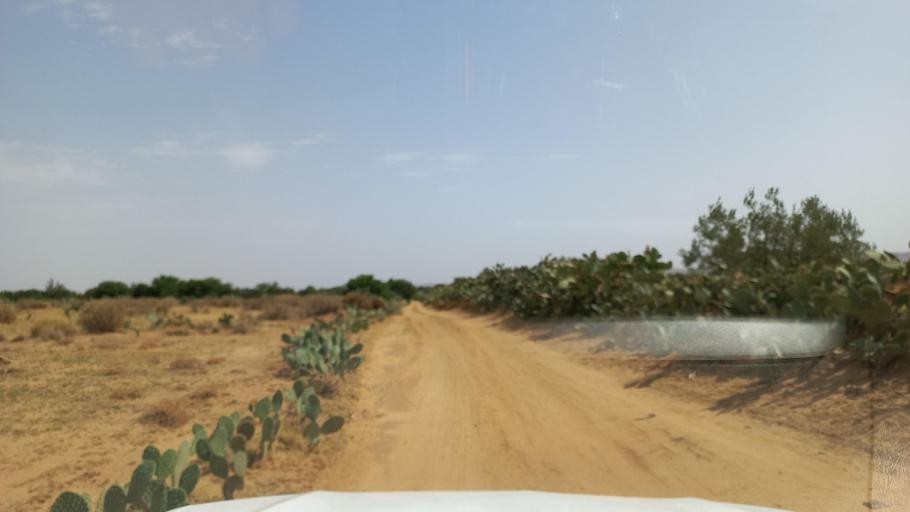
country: TN
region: Al Qasrayn
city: Kasserine
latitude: 35.2450
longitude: 9.0660
